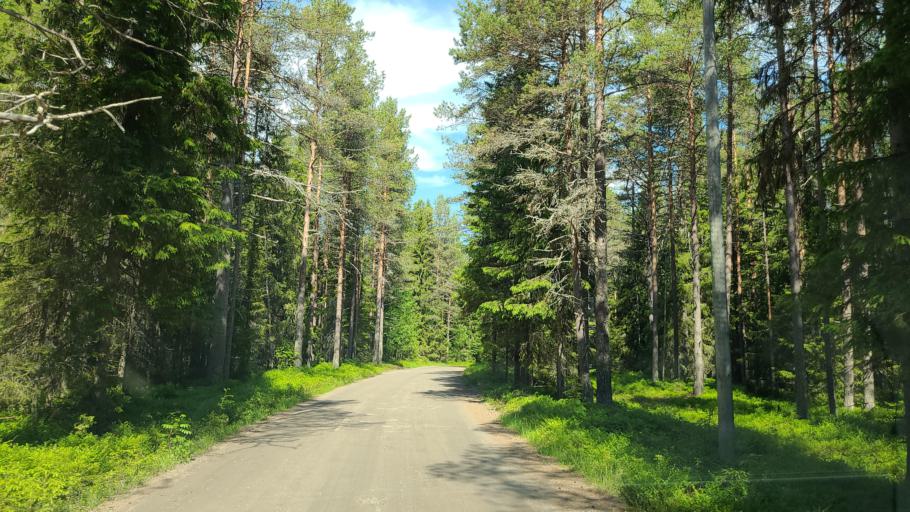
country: SE
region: Vaesterbotten
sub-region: Robertsfors Kommun
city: Robertsfors
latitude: 64.1415
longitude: 20.9607
